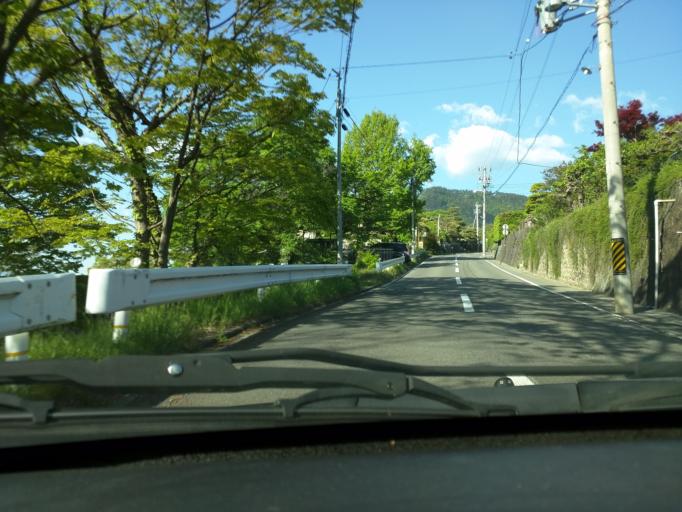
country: JP
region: Nagano
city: Nagano-shi
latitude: 36.6620
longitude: 138.1812
